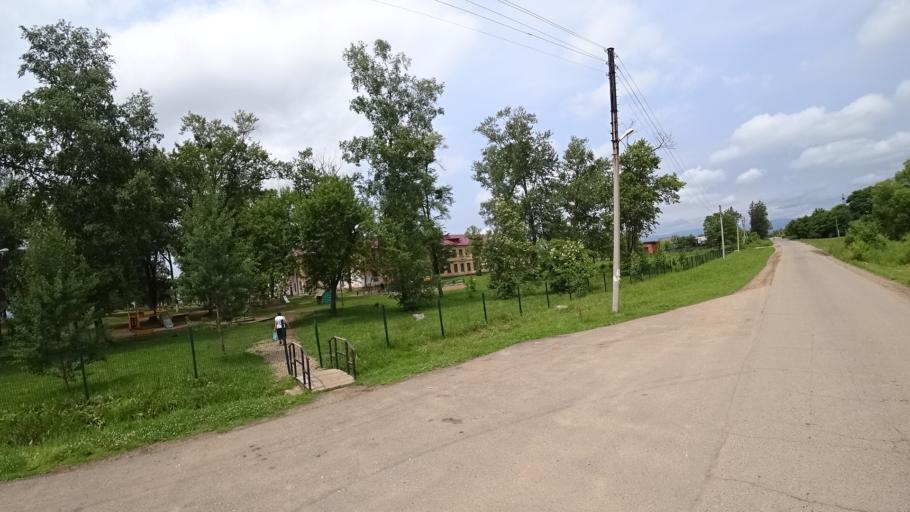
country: RU
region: Primorskiy
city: Novosysoyevka
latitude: 44.2296
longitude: 133.3610
